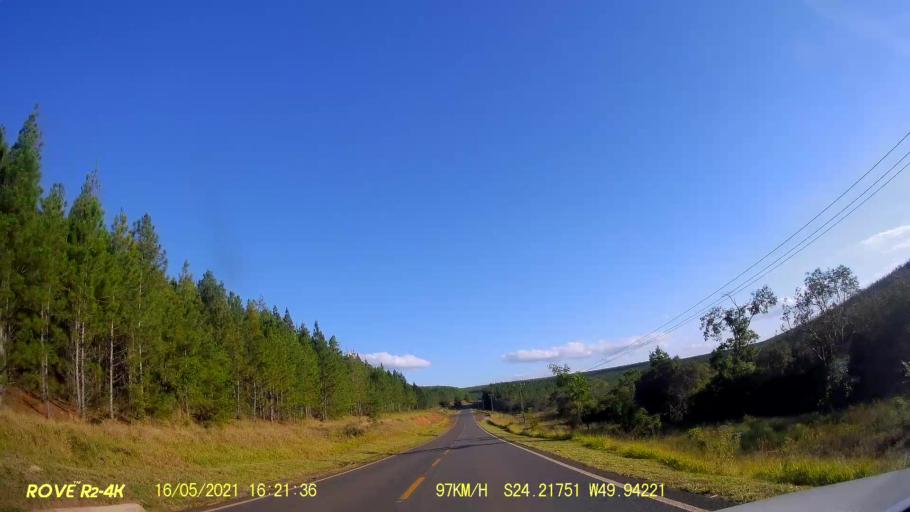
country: BR
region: Parana
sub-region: Jaguariaiva
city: Jaguariaiva
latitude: -24.2178
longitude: -49.9423
